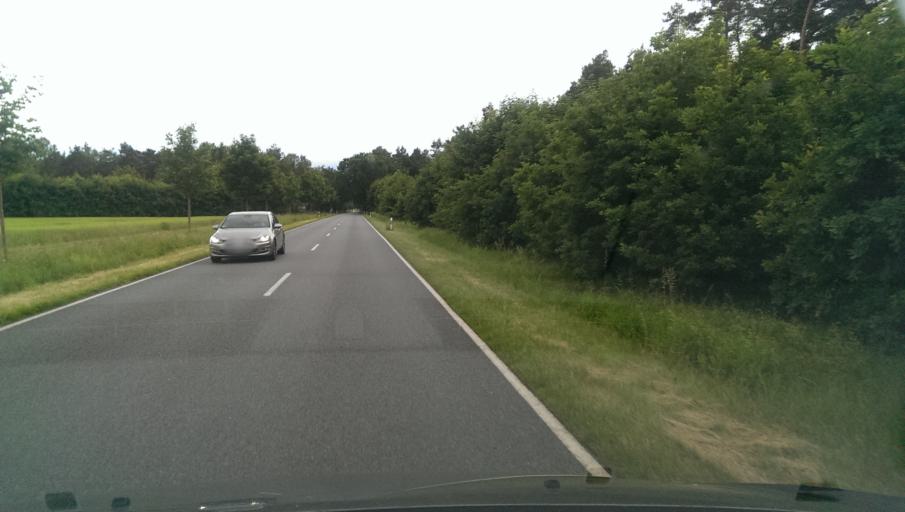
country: DE
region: Lower Saxony
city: Brome
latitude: 52.5636
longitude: 10.9279
